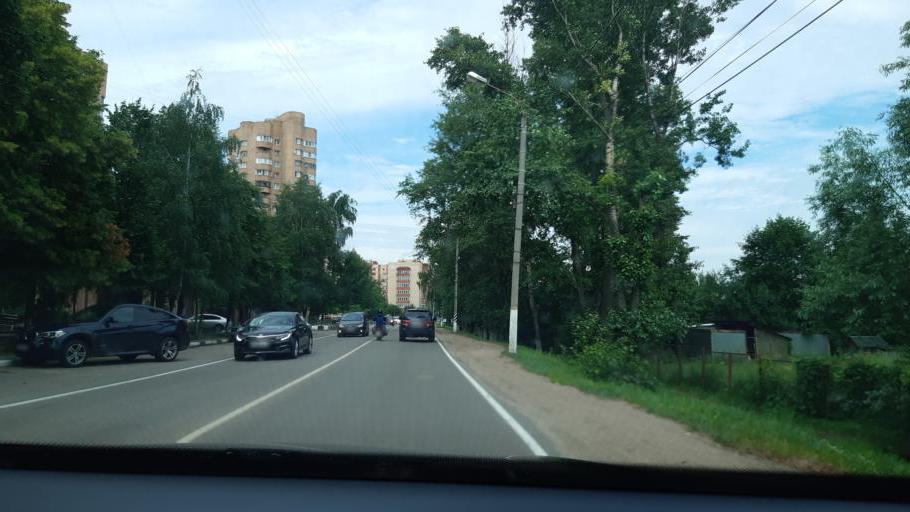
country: RU
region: Moskovskaya
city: Bol'shiye Vyazemy
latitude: 55.6227
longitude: 36.9840
